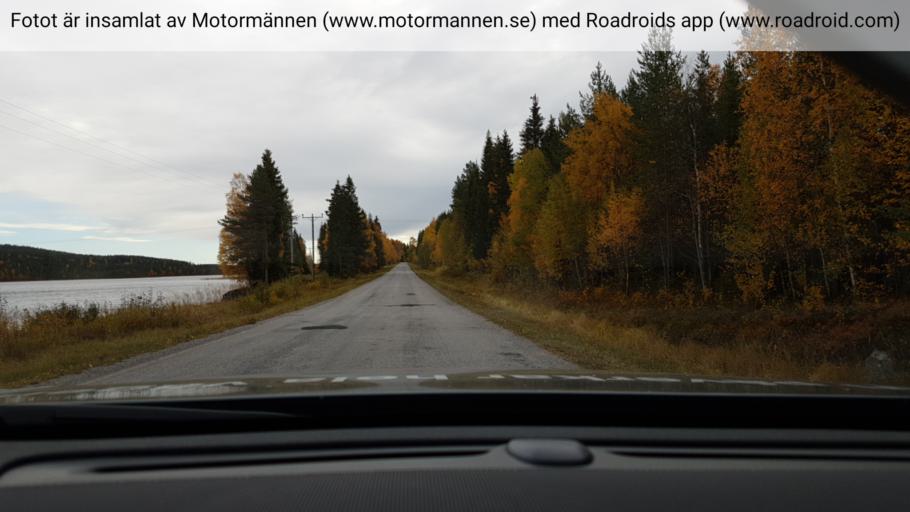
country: SE
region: Norrbotten
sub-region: Overkalix Kommun
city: OEverkalix
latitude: 66.2419
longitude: 23.0041
